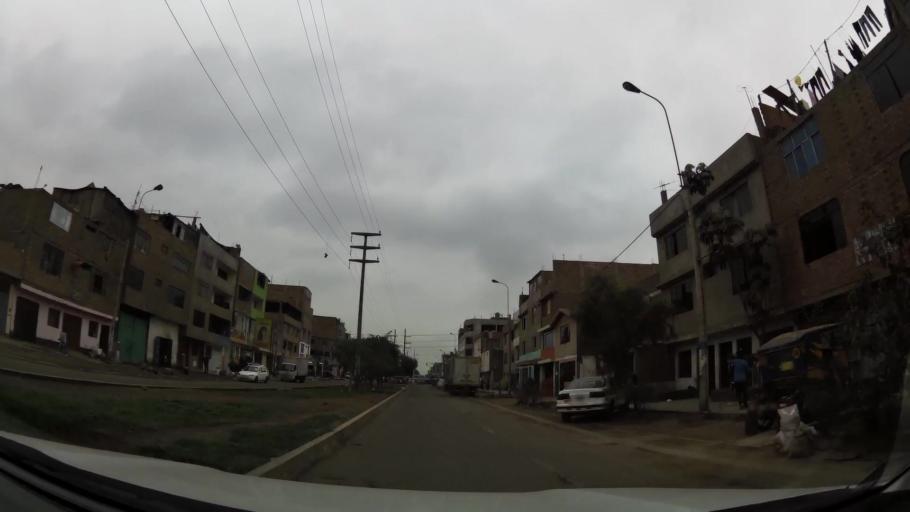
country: PE
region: Lima
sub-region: Lima
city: Vitarte
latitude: -12.0369
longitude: -76.9659
